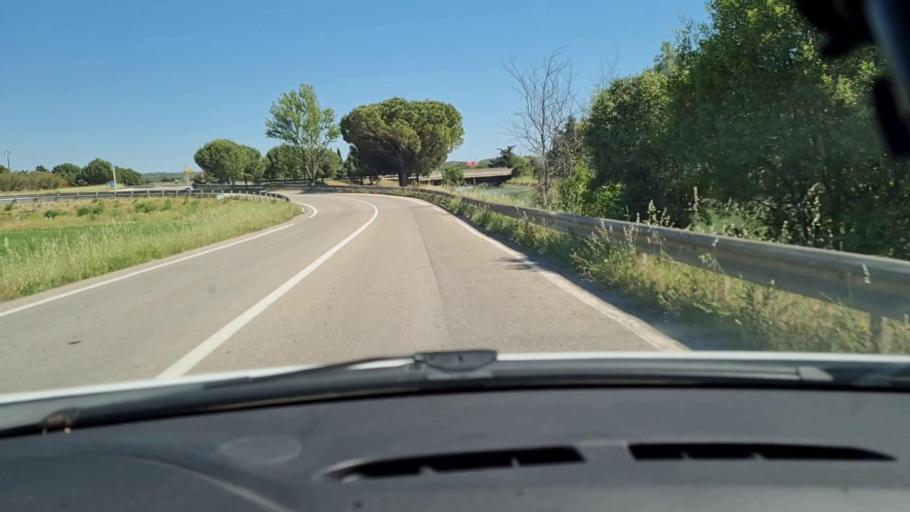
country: FR
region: Languedoc-Roussillon
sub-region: Departement du Gard
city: Vauvert
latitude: 43.7175
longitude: 4.2701
